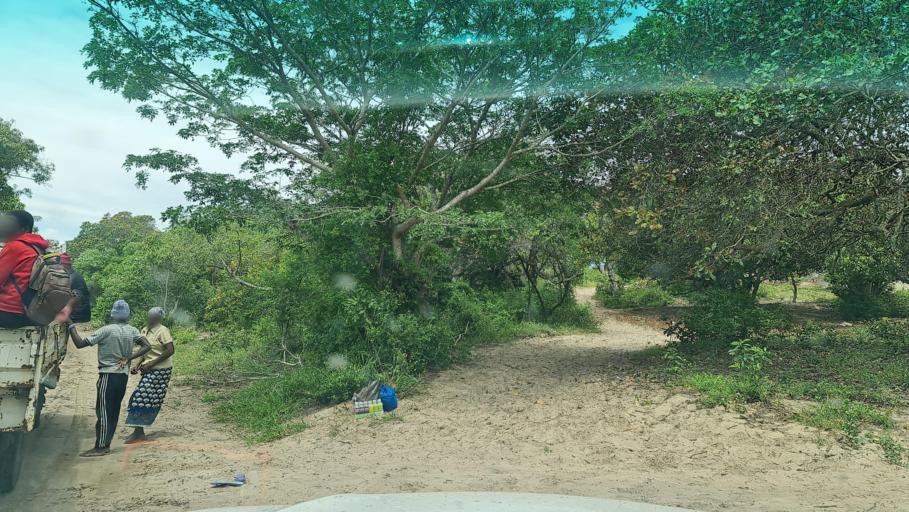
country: MZ
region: Maputo
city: Manhica
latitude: -25.5220
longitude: 32.8622
